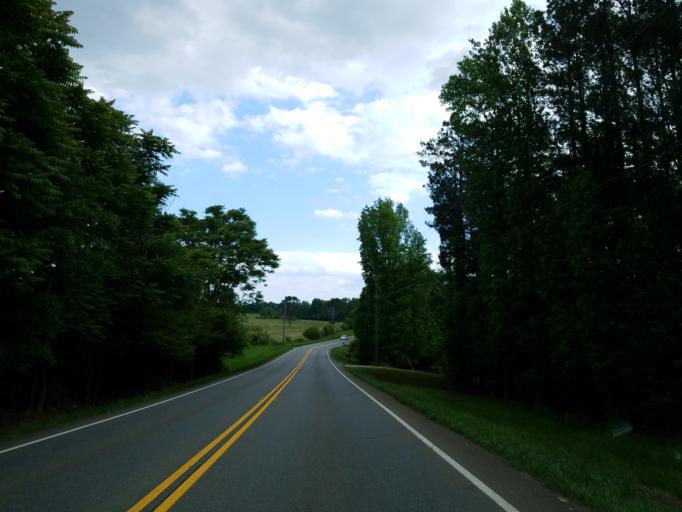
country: US
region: Georgia
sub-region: Fulton County
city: Milton
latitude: 34.2480
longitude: -84.2857
